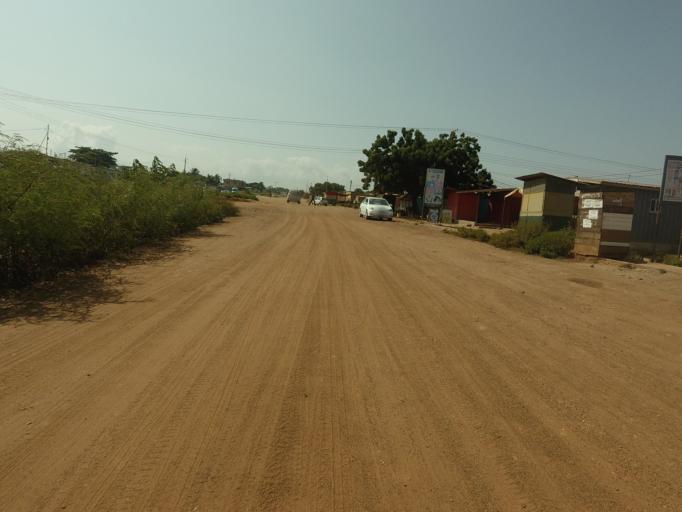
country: GH
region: Greater Accra
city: Teshi Old Town
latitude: 5.5884
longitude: -0.1152
